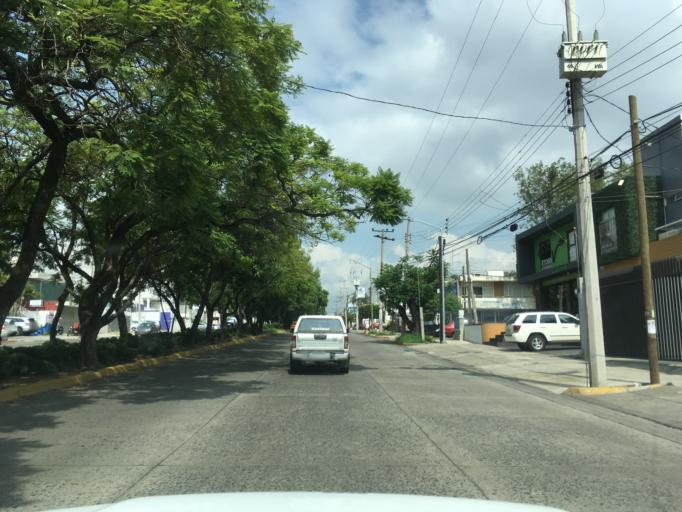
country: MX
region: Jalisco
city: Guadalajara
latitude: 20.6667
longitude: -103.3858
